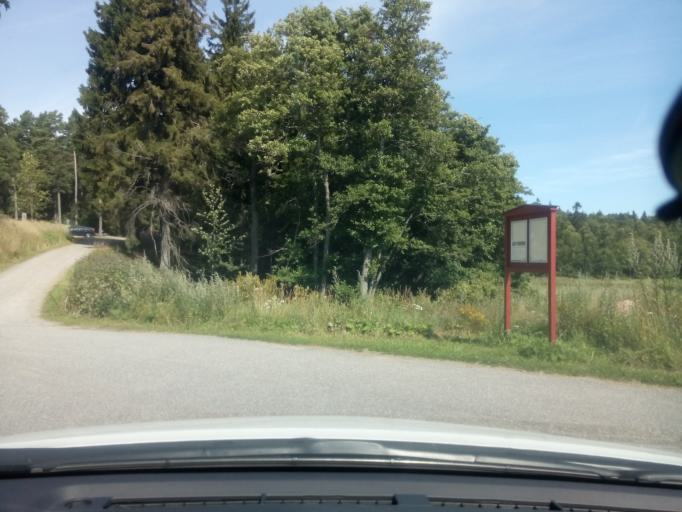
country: SE
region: Soedermanland
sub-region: Trosa Kommun
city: Trosa
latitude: 58.7951
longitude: 17.3849
